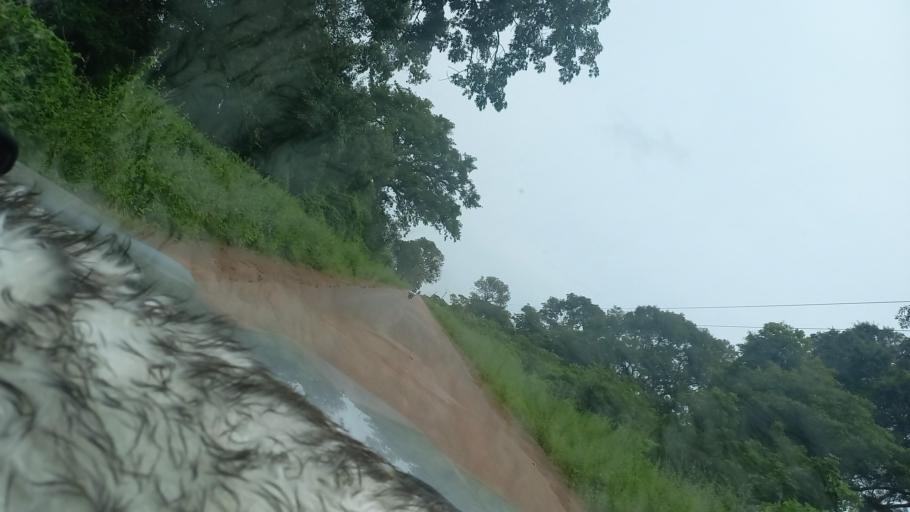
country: SN
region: Ziguinchor
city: Bignona
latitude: 12.8266
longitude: -16.1708
